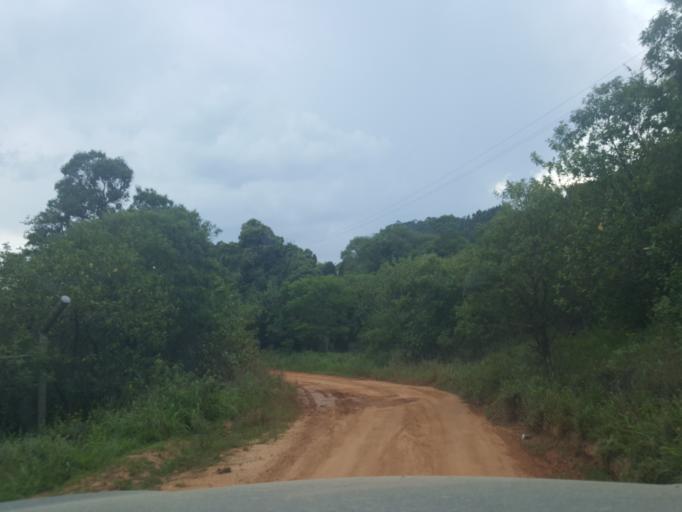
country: ZA
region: Limpopo
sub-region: Mopani District Municipality
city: Hoedspruit
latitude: -24.5765
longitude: 30.8659
